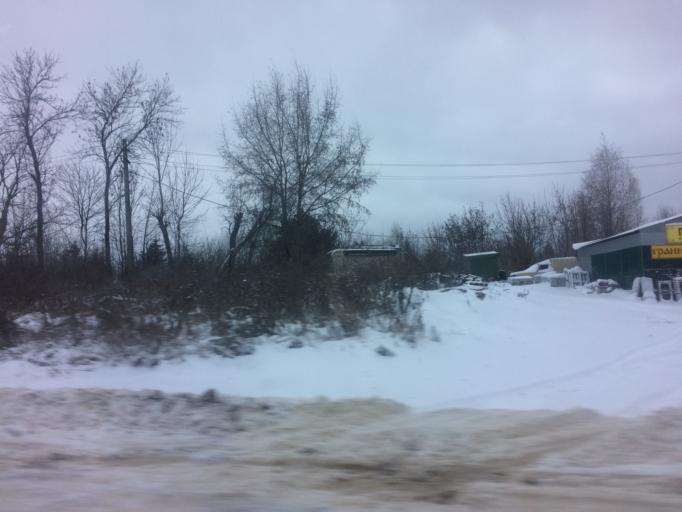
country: RU
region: Tula
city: Tula
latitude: 54.1466
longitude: 37.6469
